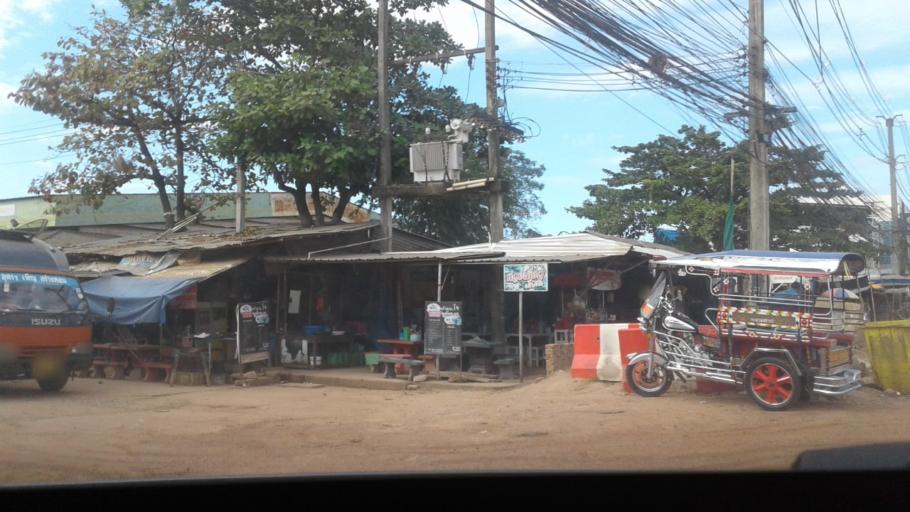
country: TH
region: Changwat Udon Thani
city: Udon Thani
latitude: 17.4327
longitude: 102.7913
